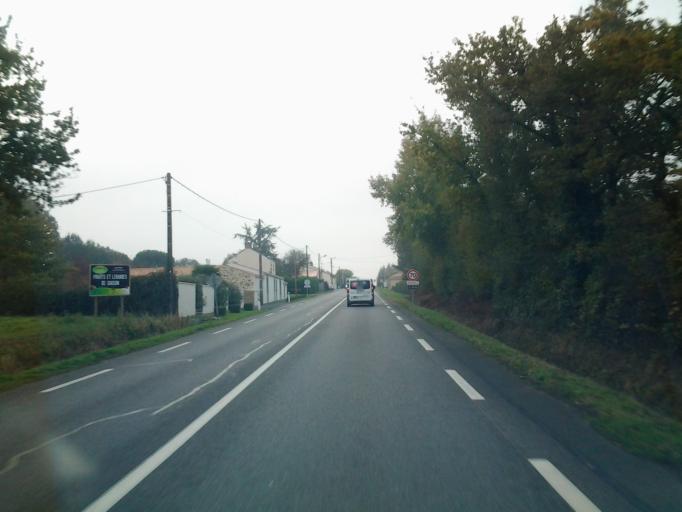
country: FR
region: Pays de la Loire
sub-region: Departement de la Vendee
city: Nesmy
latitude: 46.6206
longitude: -1.3645
